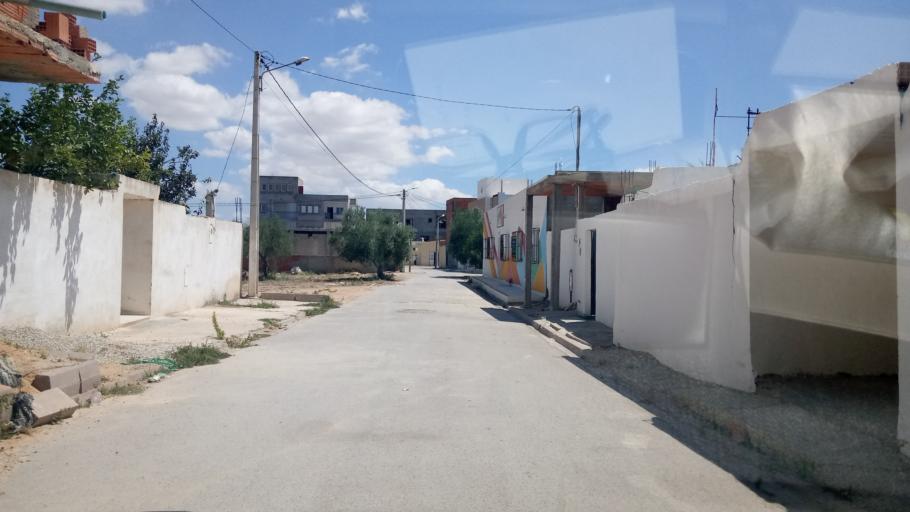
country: TN
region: Al Qayrawan
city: Sbikha
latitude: 36.1259
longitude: 10.0897
